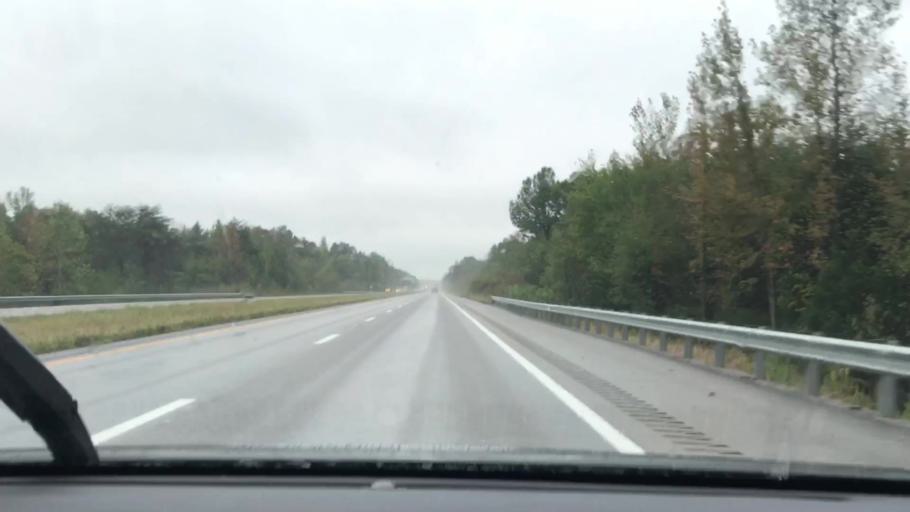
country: US
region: Kentucky
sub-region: Hopkins County
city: Nortonville
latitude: 37.1695
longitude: -87.4519
